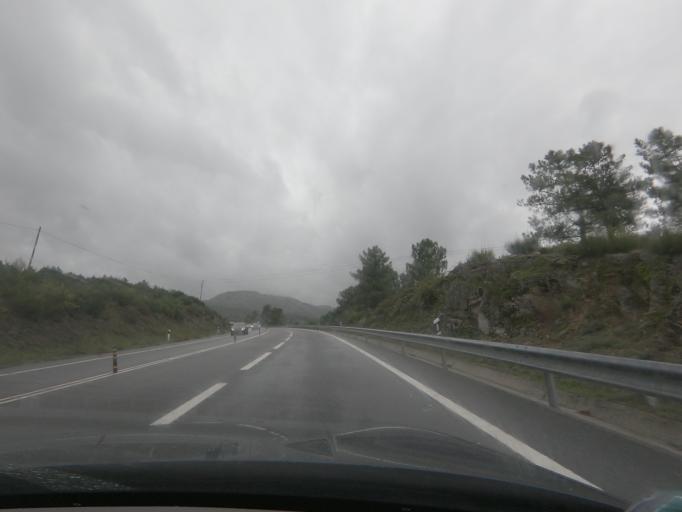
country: PT
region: Vila Real
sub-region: Vila Real
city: Vila Real
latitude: 41.2793
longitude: -7.7975
